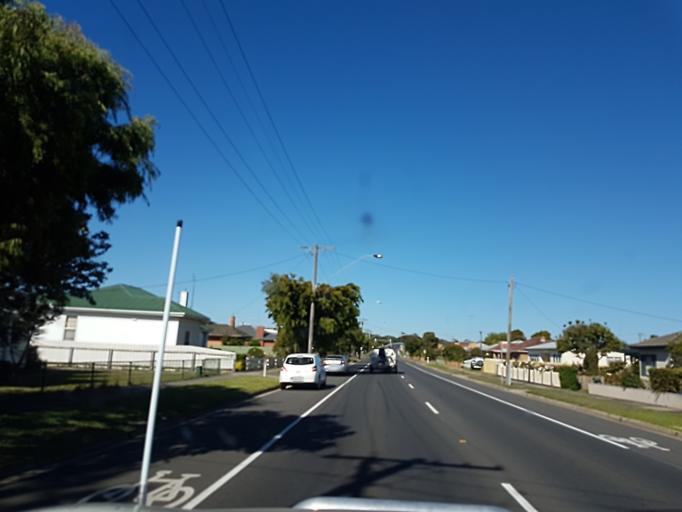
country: AU
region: Victoria
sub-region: Colac-Otway
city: Colac
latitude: -38.3369
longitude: 143.6009
